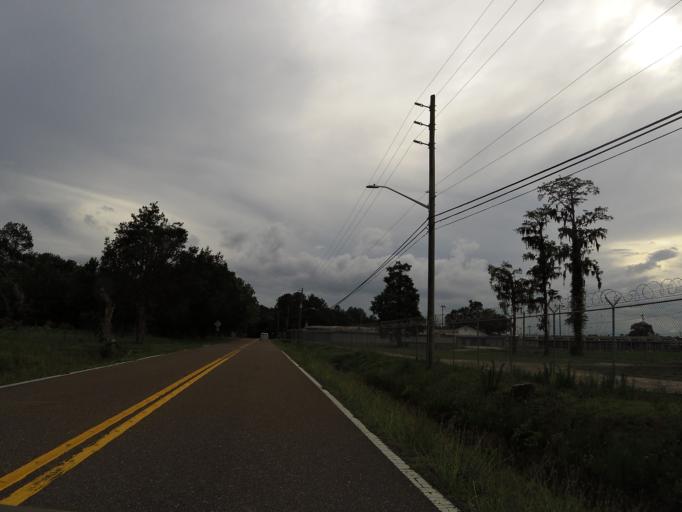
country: US
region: Florida
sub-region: Nassau County
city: Nassau Village-Ratliff
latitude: 30.5394
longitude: -81.7229
